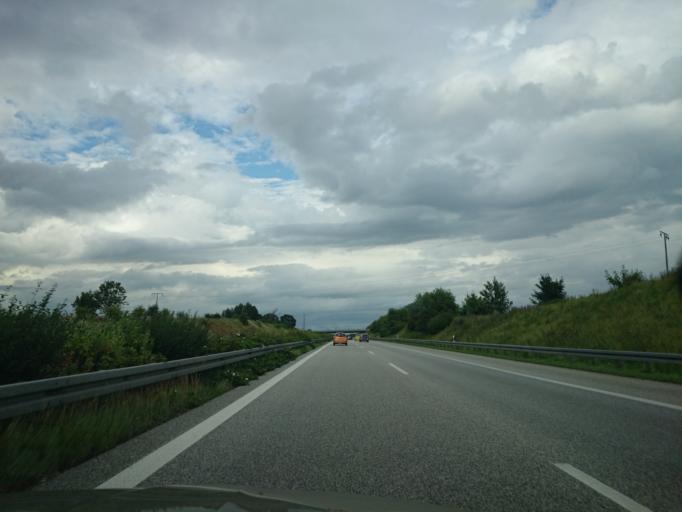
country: DE
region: Mecklenburg-Vorpommern
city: Bernitt
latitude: 53.9381
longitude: 11.8275
